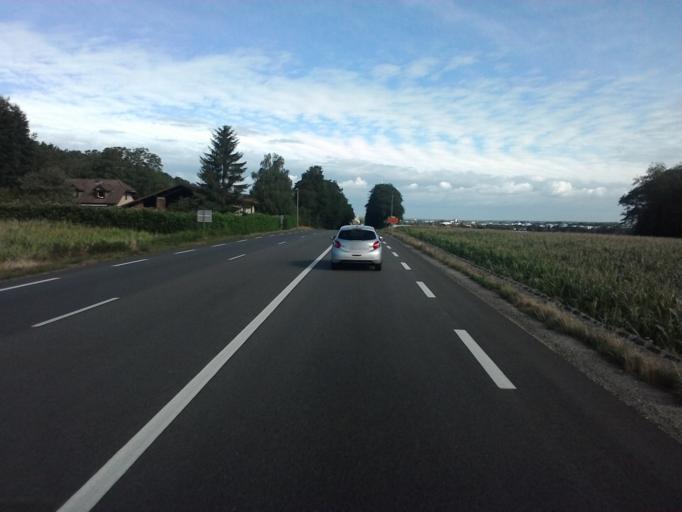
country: FR
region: Rhone-Alpes
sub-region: Departement de l'Ain
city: Bourg-en-Bresse
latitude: 46.1808
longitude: 5.2522
